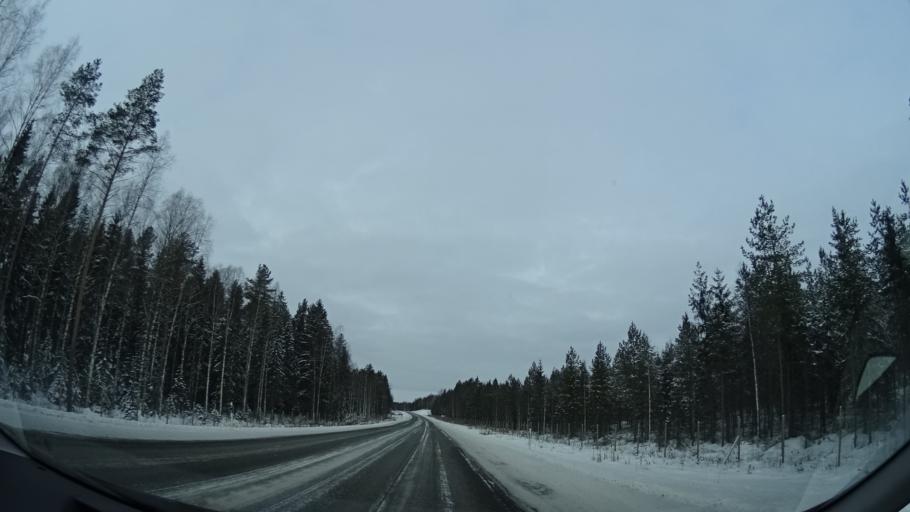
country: FI
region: Uusimaa
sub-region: Helsinki
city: Kaerkoelae
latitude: 60.6158
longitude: 24.0236
